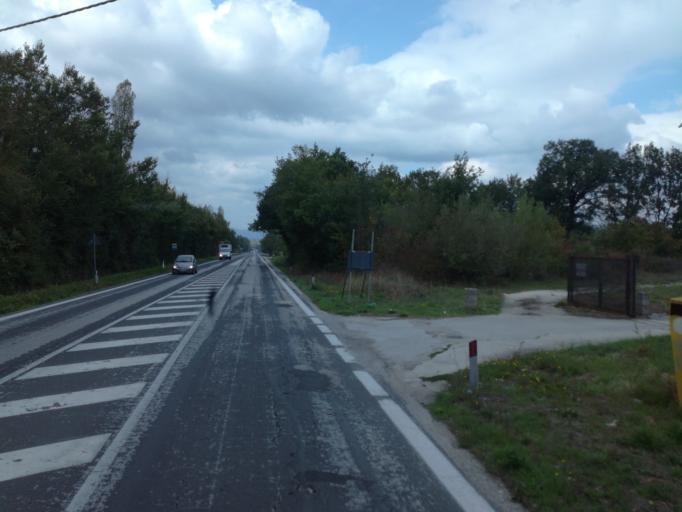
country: IT
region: Molise
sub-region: Provincia di Campobasso
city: San Polomatese
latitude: 41.4762
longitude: 14.5072
